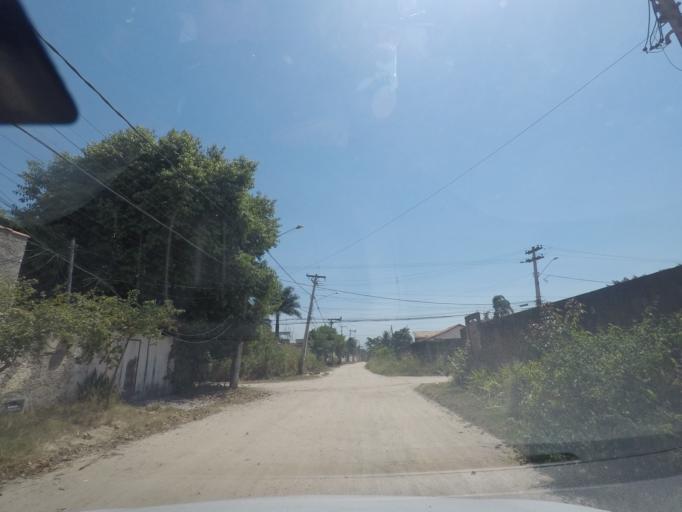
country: BR
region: Rio de Janeiro
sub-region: Niteroi
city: Niteroi
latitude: -22.9342
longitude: -43.0149
